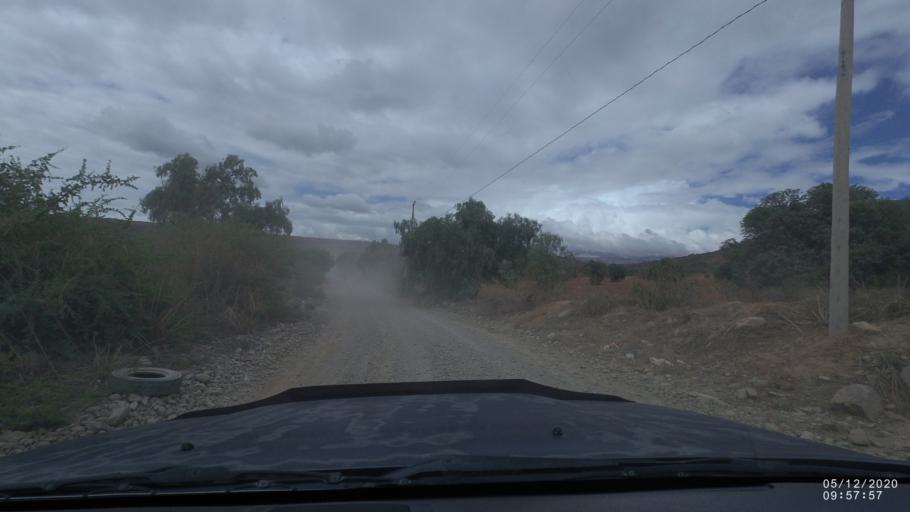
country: BO
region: Cochabamba
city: Sipe Sipe
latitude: -17.4262
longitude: -66.2904
